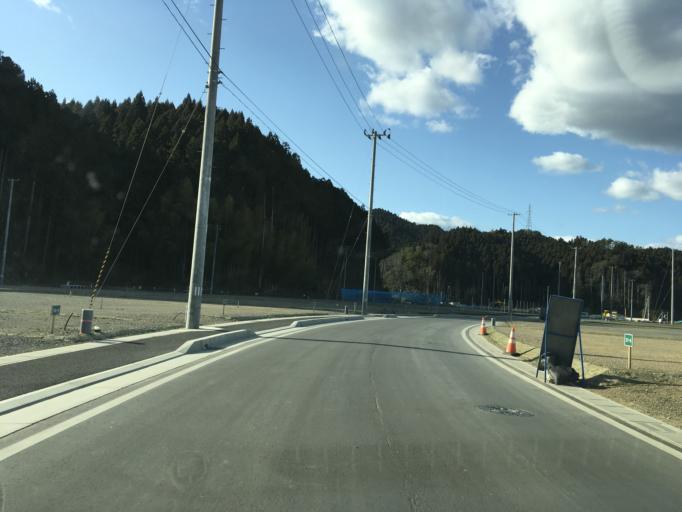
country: JP
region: Iwate
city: Ofunato
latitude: 39.0135
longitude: 141.6152
